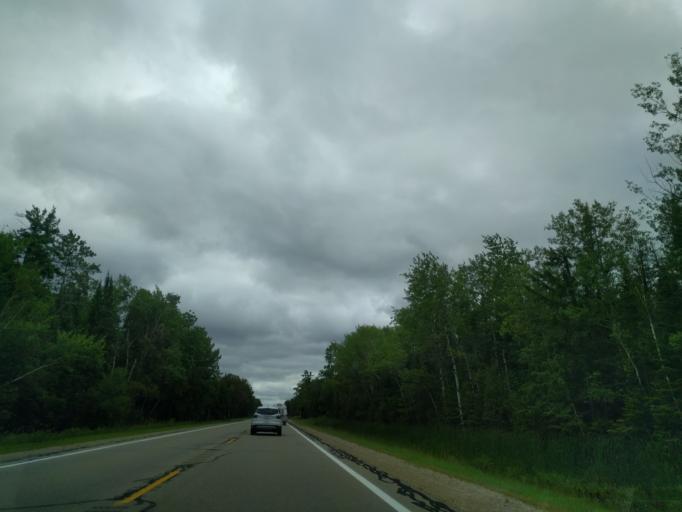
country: US
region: Michigan
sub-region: Menominee County
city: Menominee
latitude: 45.3470
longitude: -87.4091
